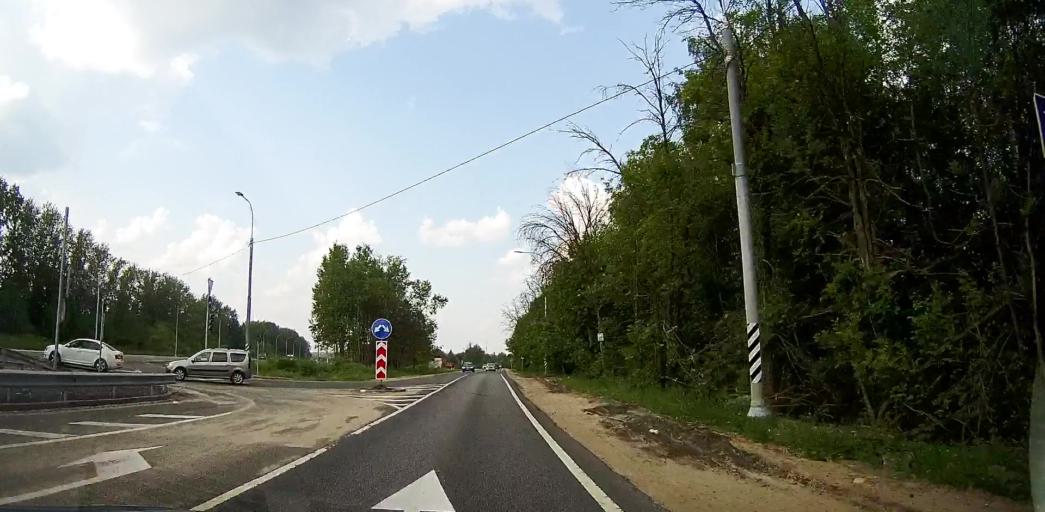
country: RU
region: Moskovskaya
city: Mikhnevo
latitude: 55.1049
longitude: 37.9457
